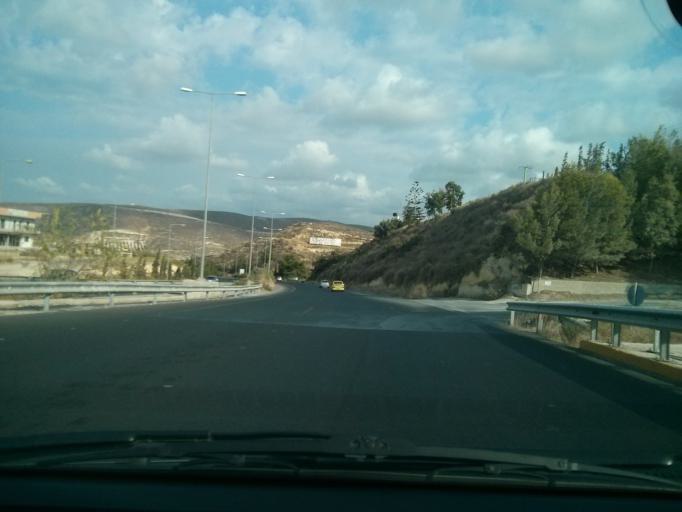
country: GR
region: Crete
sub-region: Nomos Irakleiou
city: Nea Alikarnassos
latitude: 35.3219
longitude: 25.1844
